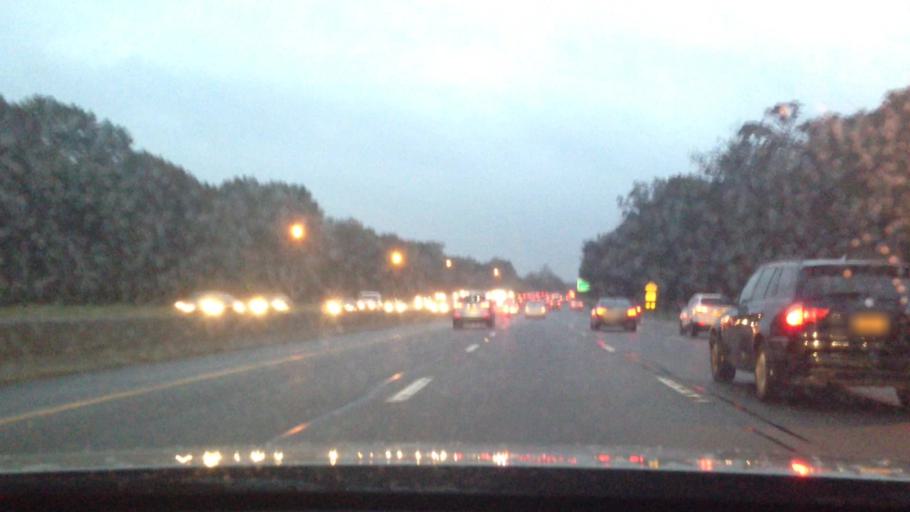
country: US
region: New York
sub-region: Nassau County
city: Malverne
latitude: 40.6829
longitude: -73.6717
